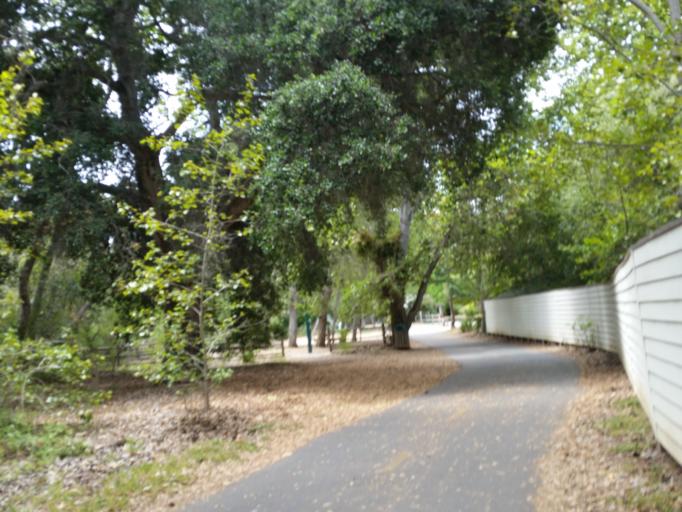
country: US
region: California
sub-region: San Luis Obispo County
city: Avila Beach
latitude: 35.1891
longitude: -120.7216
